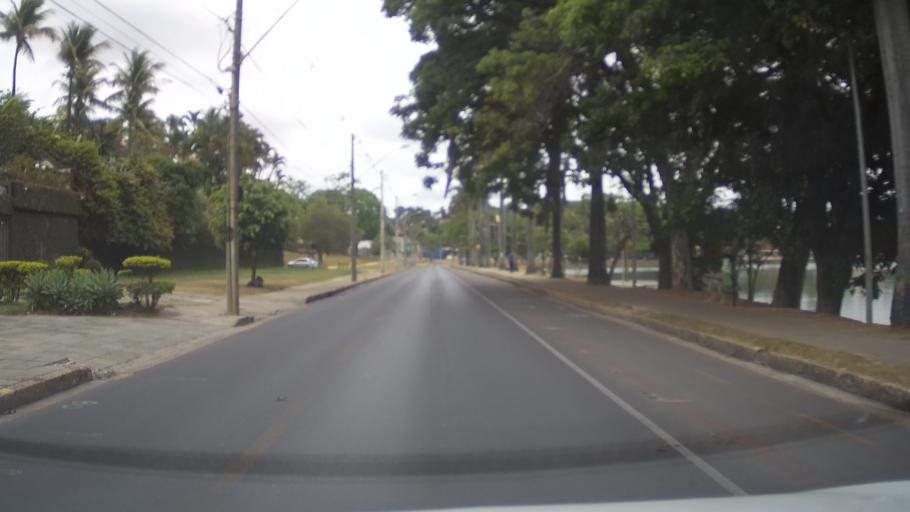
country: BR
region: Minas Gerais
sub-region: Belo Horizonte
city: Belo Horizonte
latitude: -19.8521
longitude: -43.9679
